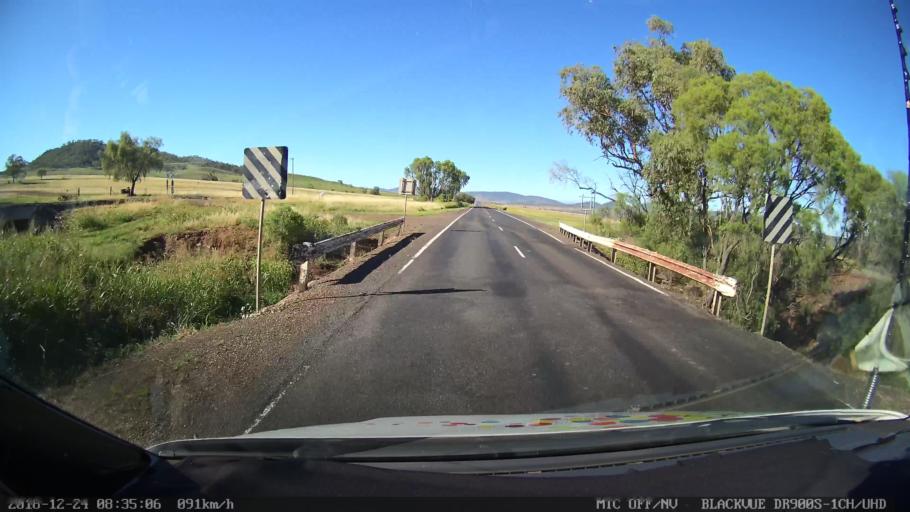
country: AU
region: New South Wales
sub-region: Liverpool Plains
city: Quirindi
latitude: -31.2985
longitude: 150.6622
